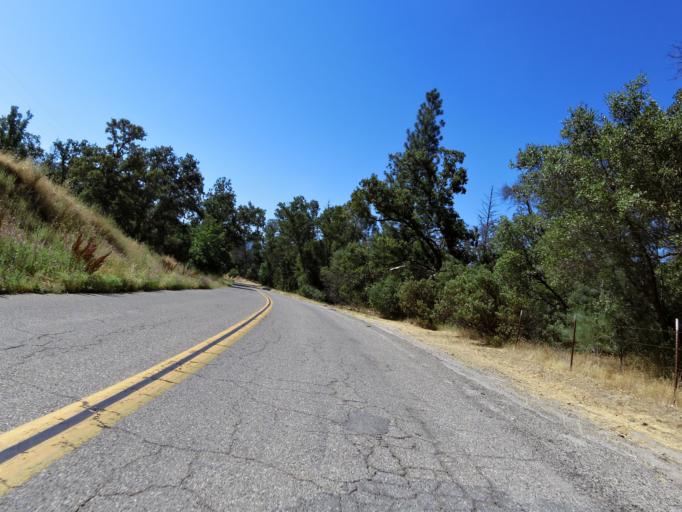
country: US
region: California
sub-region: Fresno County
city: Auberry
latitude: 37.2027
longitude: -119.4715
